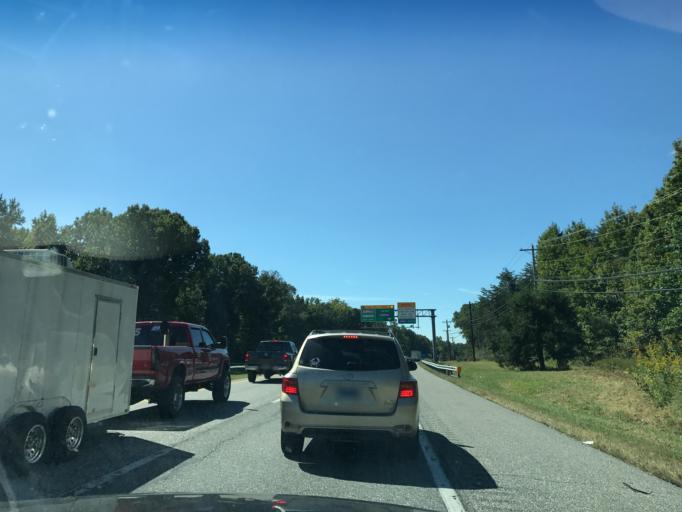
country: US
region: Virginia
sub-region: King George County
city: Dahlgren
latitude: 38.3738
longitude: -76.9585
